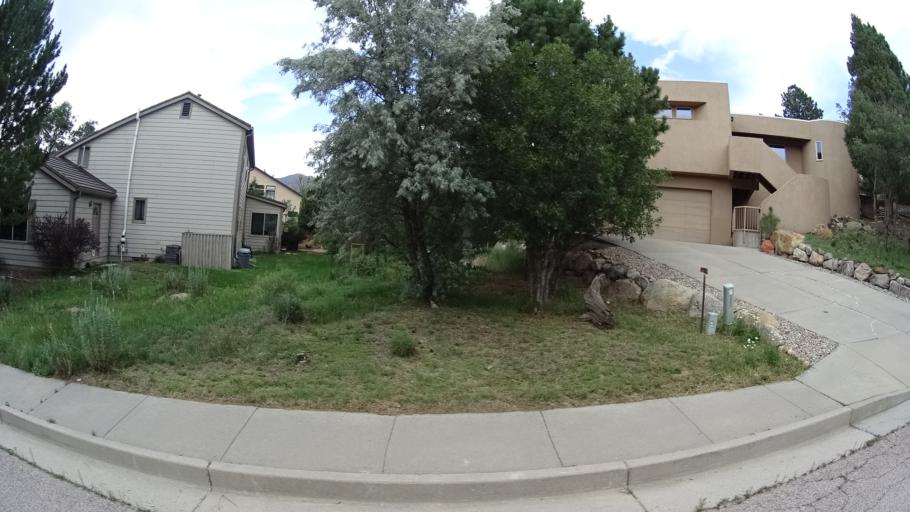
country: US
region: Colorado
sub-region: El Paso County
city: Colorado Springs
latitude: 38.9100
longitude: -104.8427
